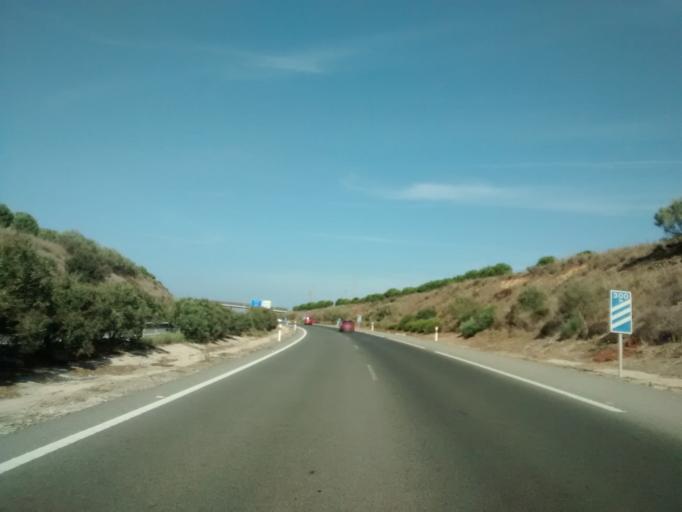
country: ES
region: Andalusia
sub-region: Provincia de Cadiz
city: Conil de la Frontera
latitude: 36.3446
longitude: -6.0539
